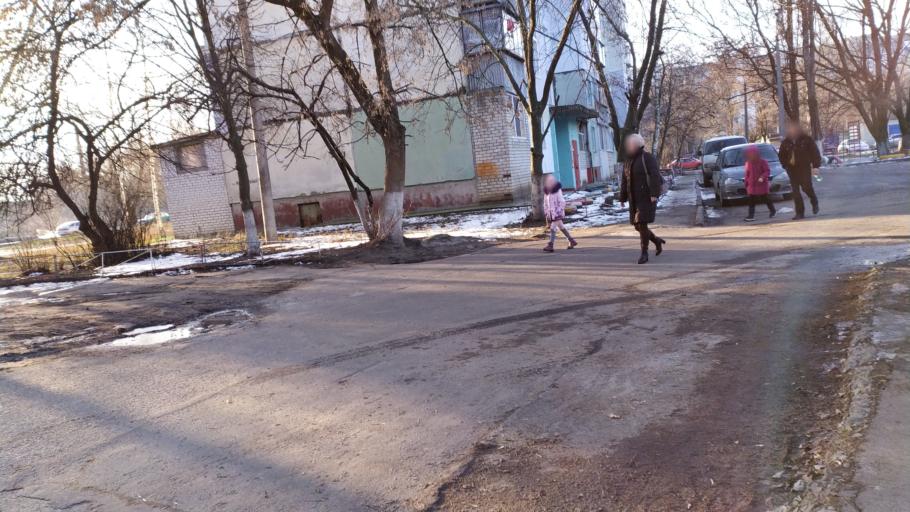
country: RU
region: Kursk
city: Kursk
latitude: 51.6501
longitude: 36.1377
